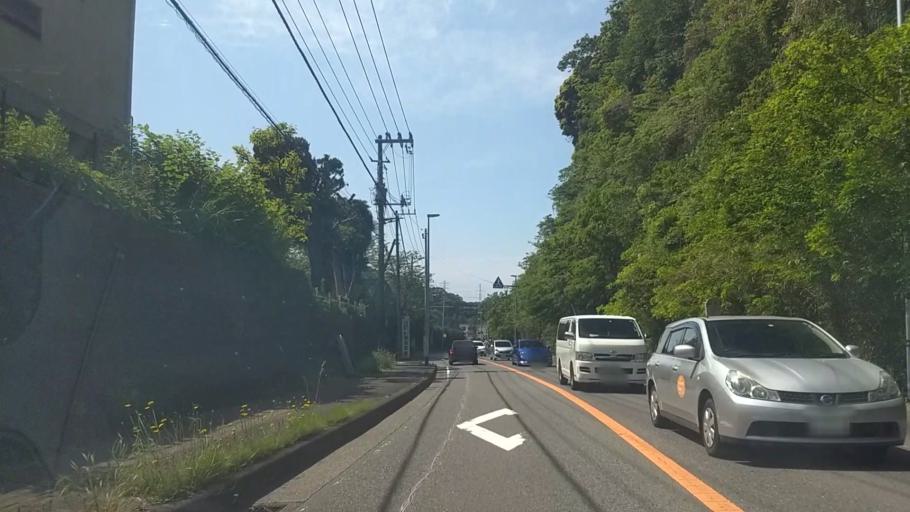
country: JP
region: Kanagawa
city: Kamakura
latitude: 35.3384
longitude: 139.5852
